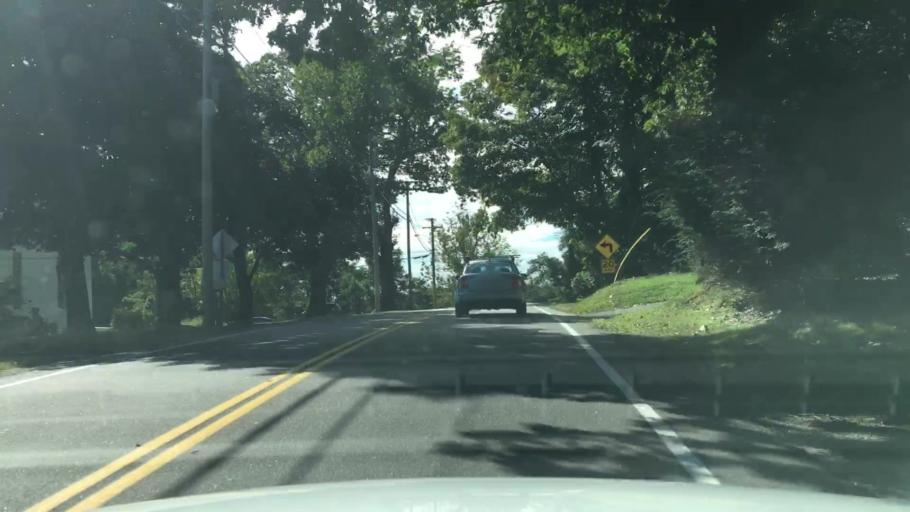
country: US
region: Maine
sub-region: York County
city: Kittery Point
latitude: 43.0823
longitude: -70.7157
